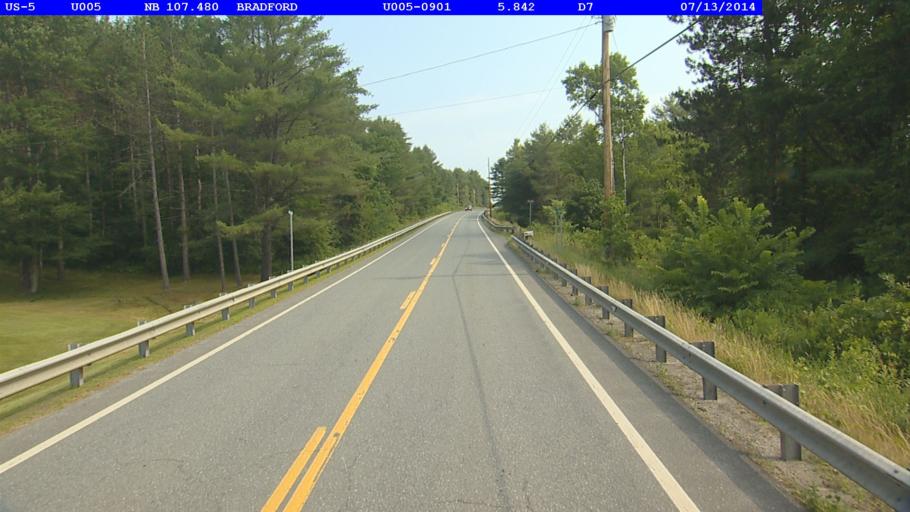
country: US
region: New Hampshire
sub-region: Grafton County
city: Haverhill
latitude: 44.0327
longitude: -72.0903
